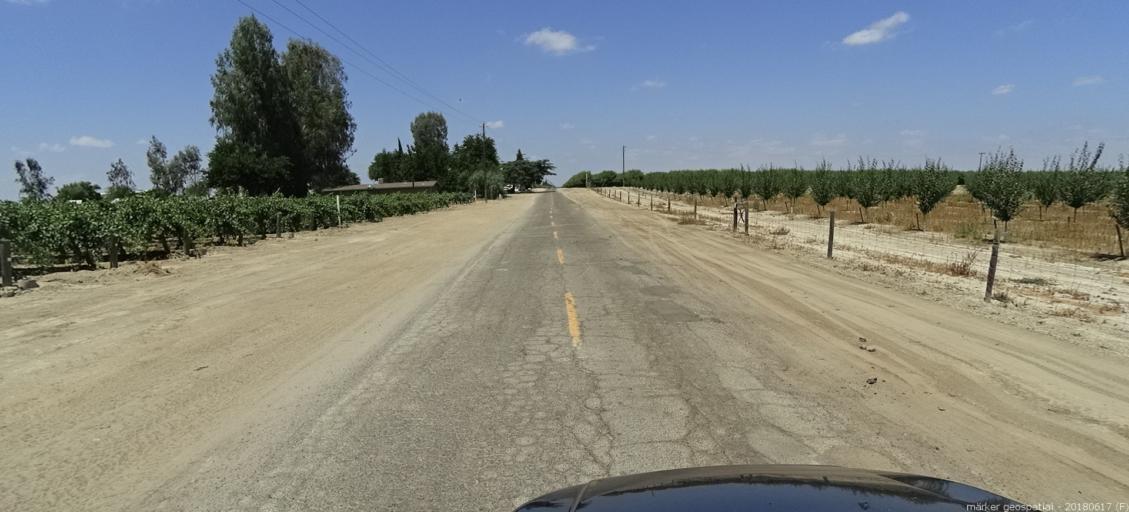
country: US
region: California
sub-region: Fresno County
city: Kerman
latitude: 36.8099
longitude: -120.1508
